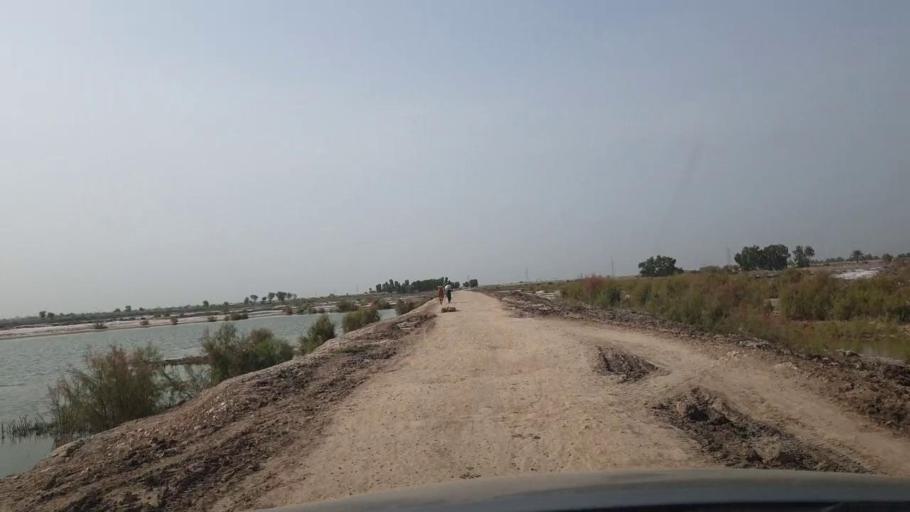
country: PK
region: Sindh
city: Lakhi
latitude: 27.8382
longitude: 68.6998
